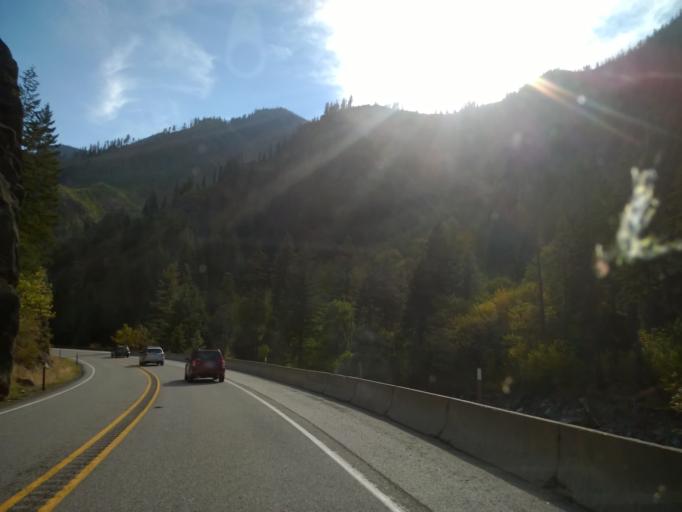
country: US
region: Washington
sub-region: Chelan County
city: Leavenworth
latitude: 47.6316
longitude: -120.7274
